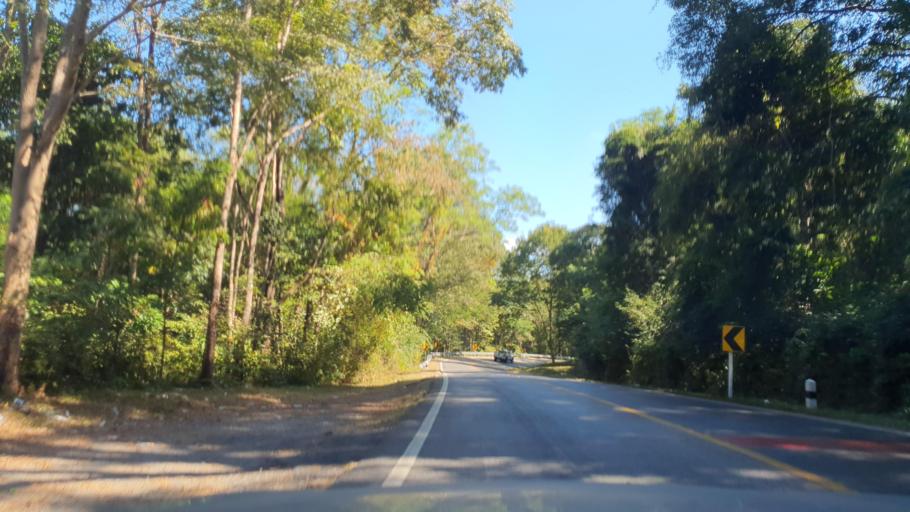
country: TH
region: Kalasin
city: Na Khu
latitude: 16.8429
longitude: 103.9076
